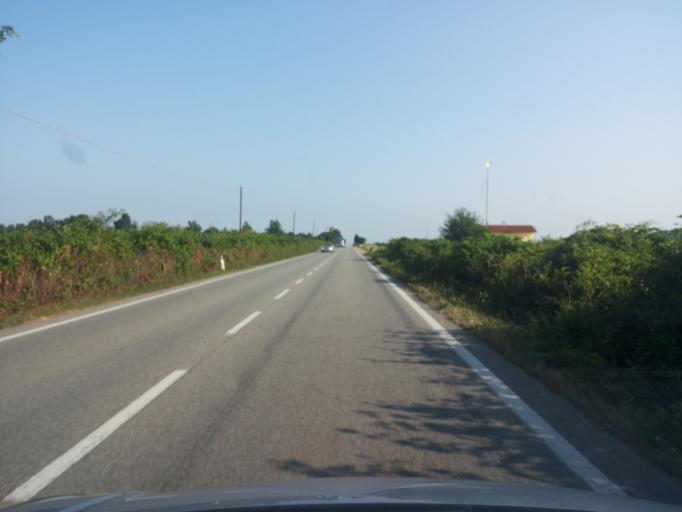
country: IT
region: Piedmont
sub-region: Provincia di Biella
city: Mottalciata
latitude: 45.4846
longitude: 8.2171
